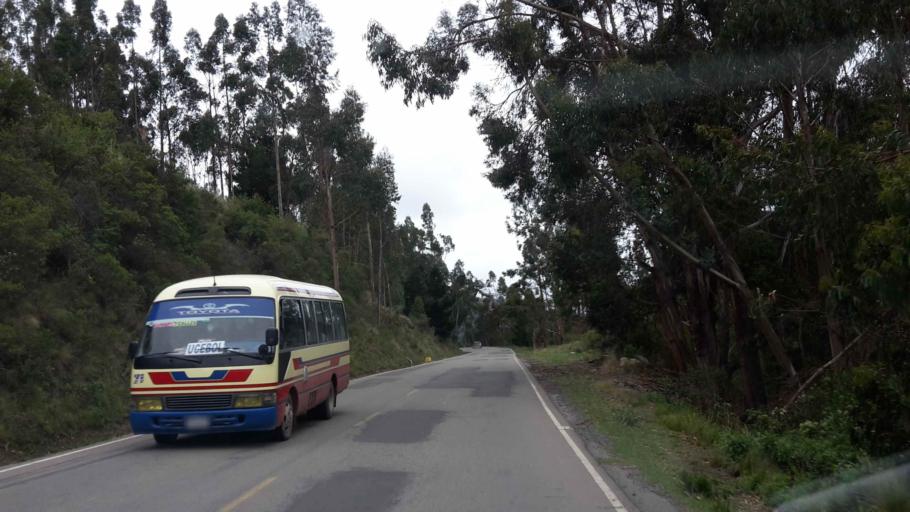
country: BO
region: Cochabamba
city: Arani
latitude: -17.4781
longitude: -65.5362
